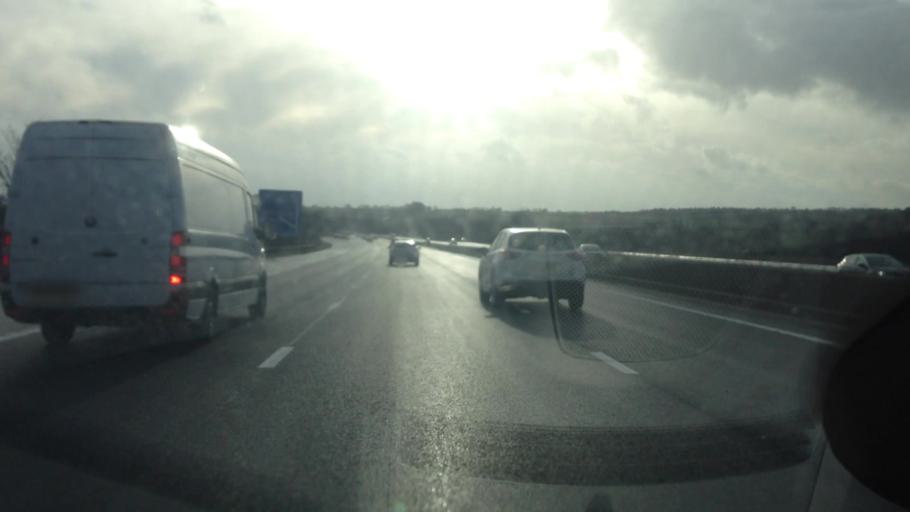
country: GB
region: England
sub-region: Barnsley
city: Darton
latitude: 53.6097
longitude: -1.5523
